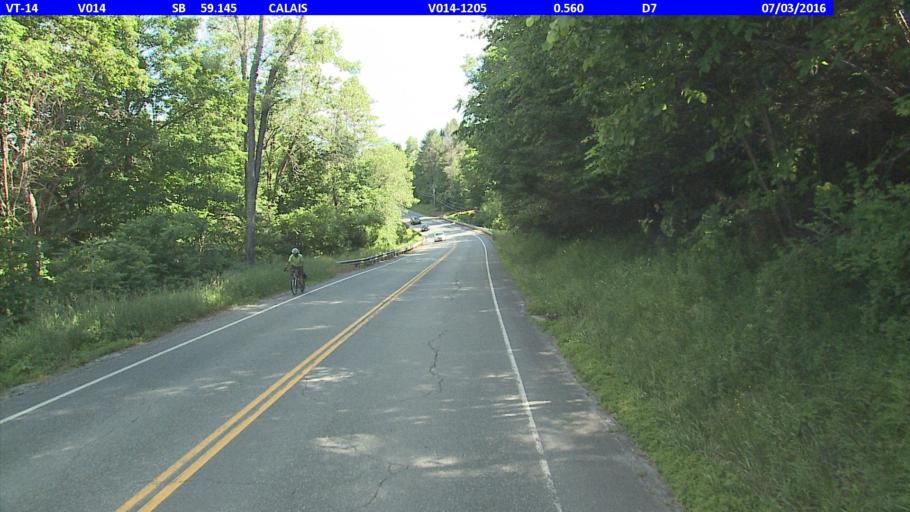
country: US
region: Vermont
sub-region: Washington County
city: Barre
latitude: 44.3153
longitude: -72.4463
